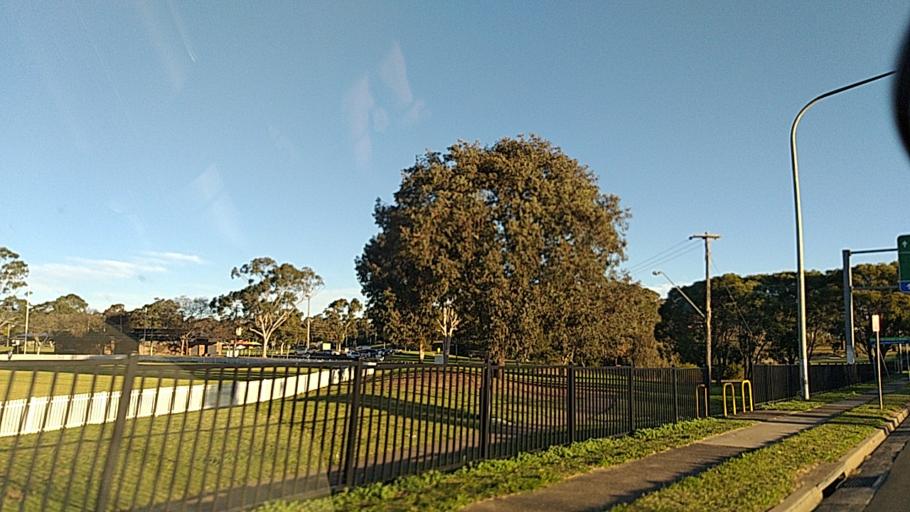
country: AU
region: New South Wales
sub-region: Campbelltown Municipality
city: Campbelltown
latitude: -34.0723
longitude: 150.8106
